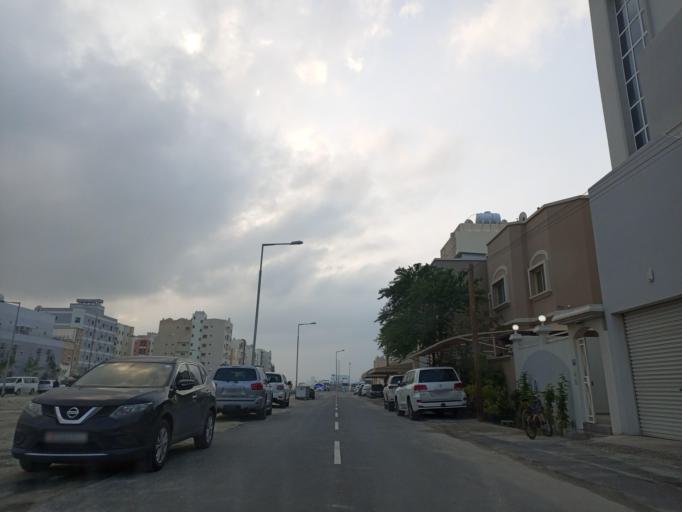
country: BH
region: Muharraq
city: Al Hadd
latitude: 26.2343
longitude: 50.6495
